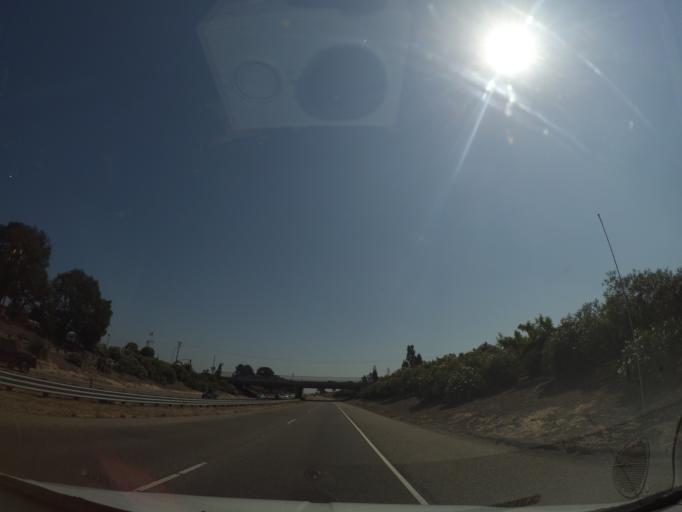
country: US
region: California
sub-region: San Luis Obispo County
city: Nipomo
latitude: 35.0379
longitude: -120.4858
